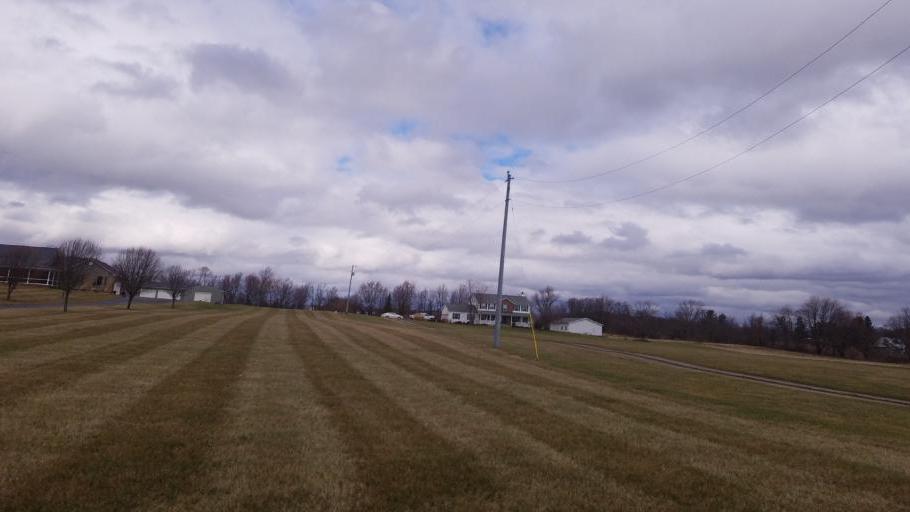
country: US
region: Ohio
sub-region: Knox County
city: Mount Vernon
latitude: 40.3339
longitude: -82.5472
